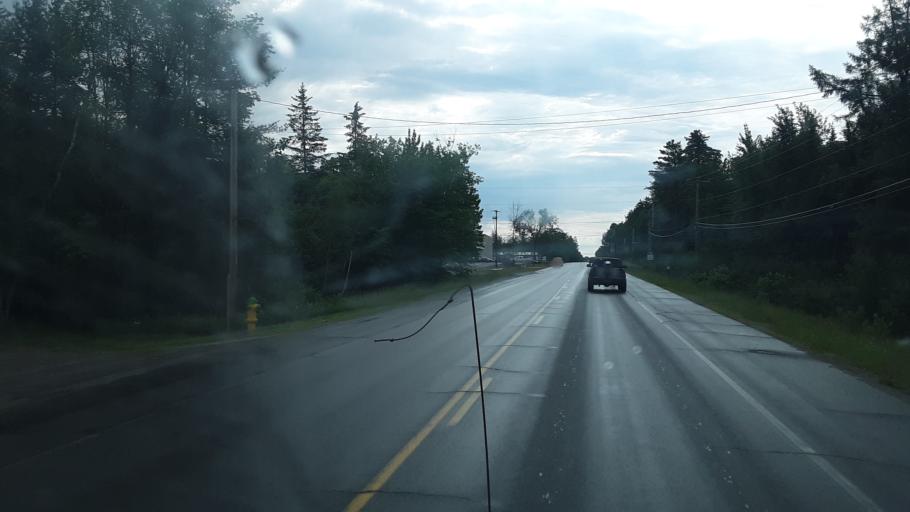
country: US
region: Maine
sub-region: Penobscot County
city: Old Town
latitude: 44.9437
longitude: -68.6749
